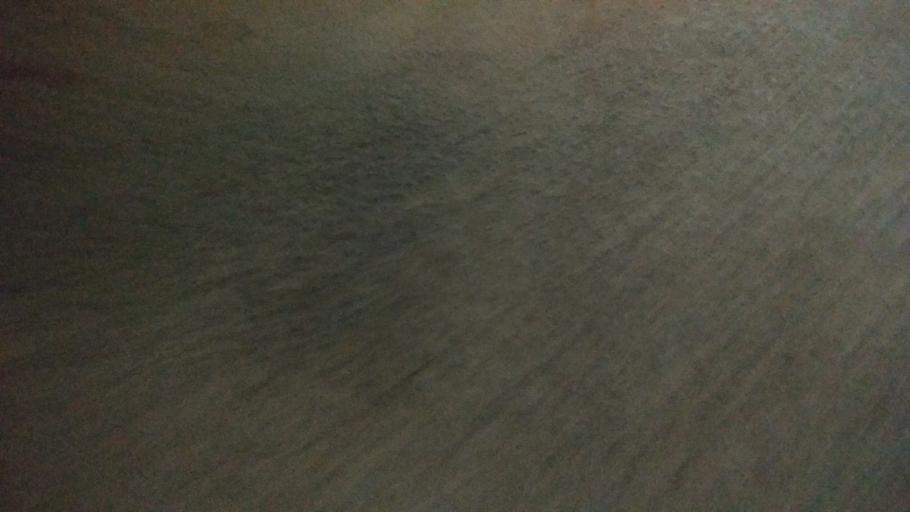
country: IN
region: Tamil Nadu
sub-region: Thiruvallur
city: Tiruvallur
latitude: 13.1232
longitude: 79.9211
